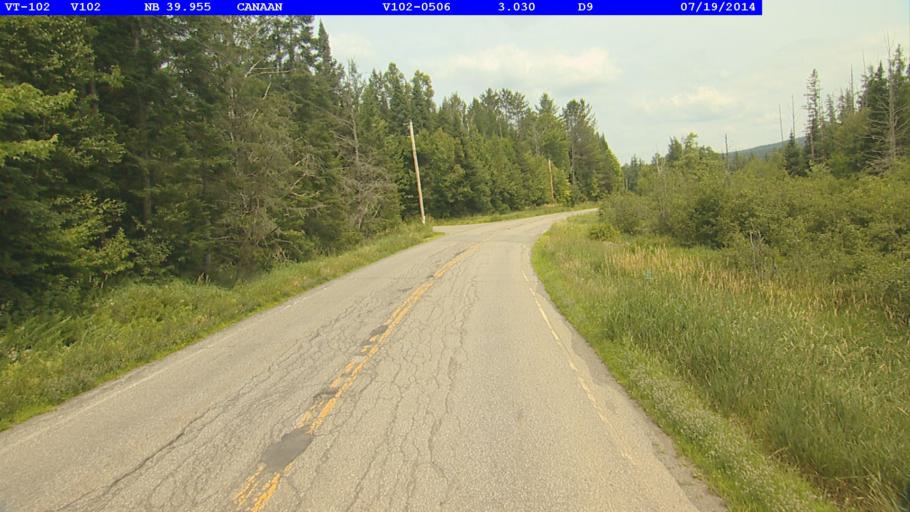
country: US
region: New Hampshire
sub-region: Coos County
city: Colebrook
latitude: 44.9500
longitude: -71.5252
